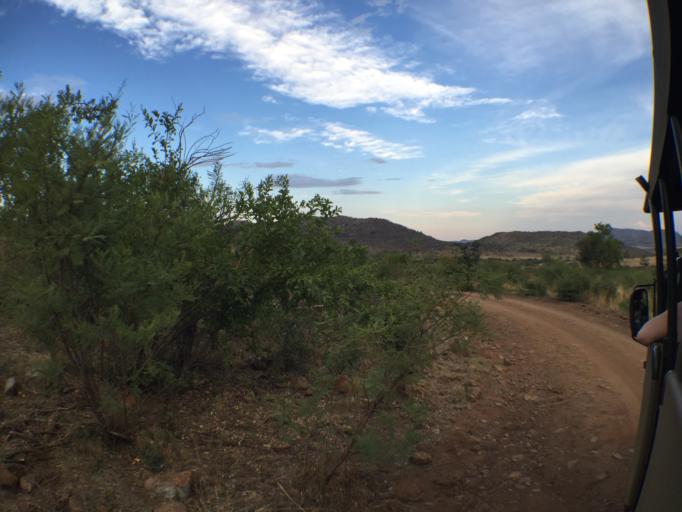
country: ZA
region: North-West
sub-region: Bojanala Platinum District Municipality
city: Mogwase
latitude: -25.2236
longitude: 27.0673
